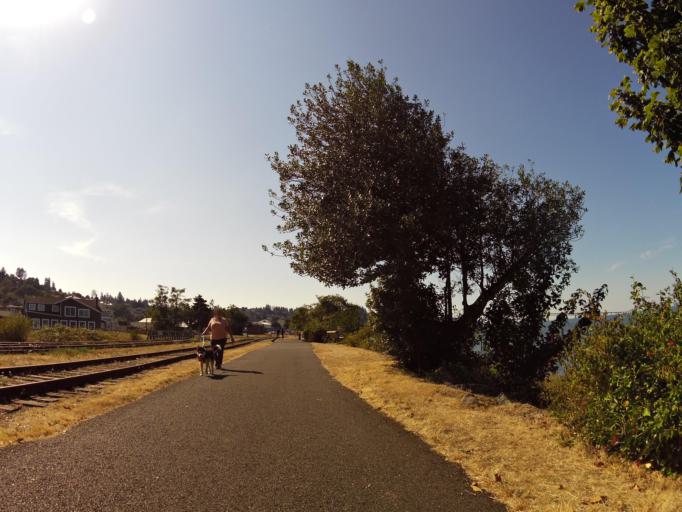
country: US
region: Oregon
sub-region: Clatsop County
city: Astoria
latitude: 46.1916
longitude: -123.8151
